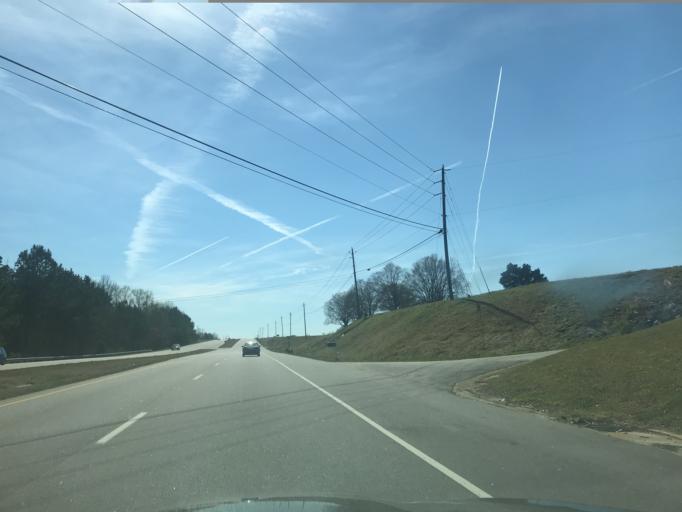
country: US
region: North Carolina
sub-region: Wake County
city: Fuquay-Varina
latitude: 35.6120
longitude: -78.7404
